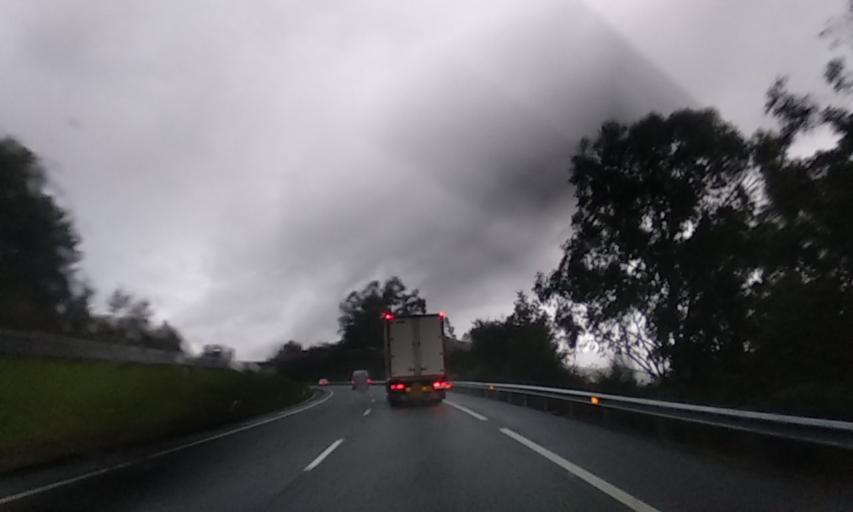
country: ES
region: Galicia
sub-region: Provincia de Pontevedra
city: Marin
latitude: 42.3423
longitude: -8.6473
